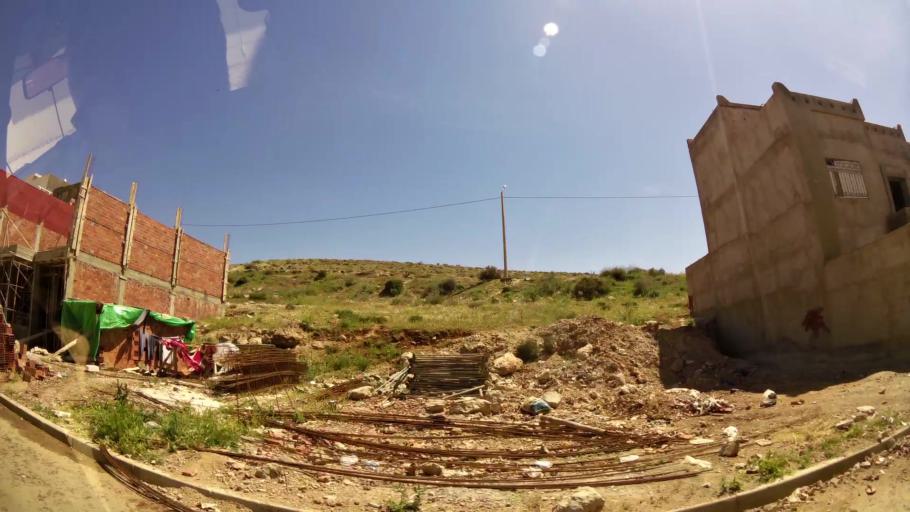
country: MA
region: Oriental
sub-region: Oujda-Angad
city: Oujda
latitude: 34.6464
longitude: -1.9069
